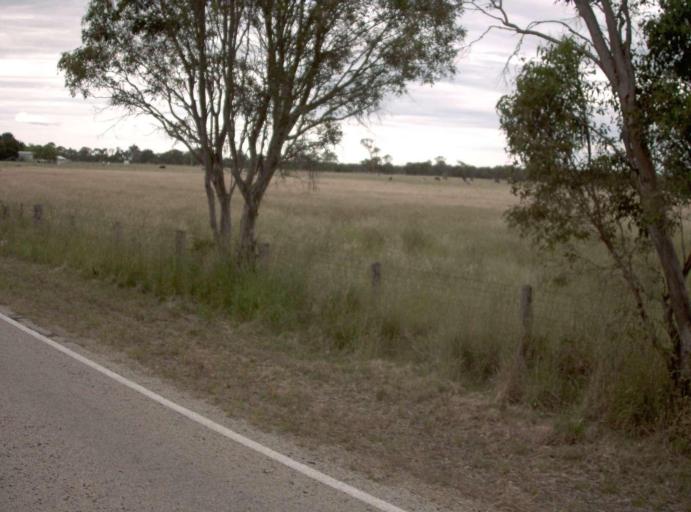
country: AU
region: Victoria
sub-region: East Gippsland
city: Bairnsdale
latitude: -37.9270
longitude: 147.5419
